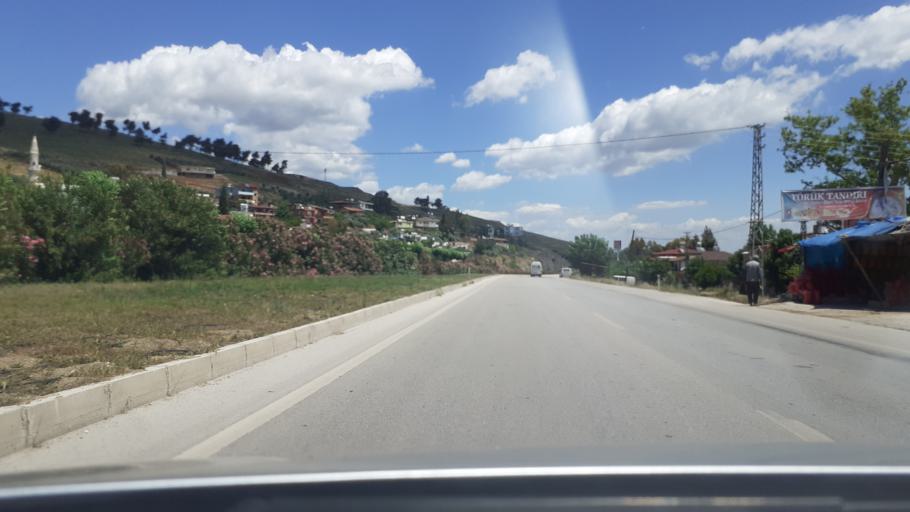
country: TR
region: Hatay
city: Serinyol
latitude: 36.4005
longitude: 36.2458
